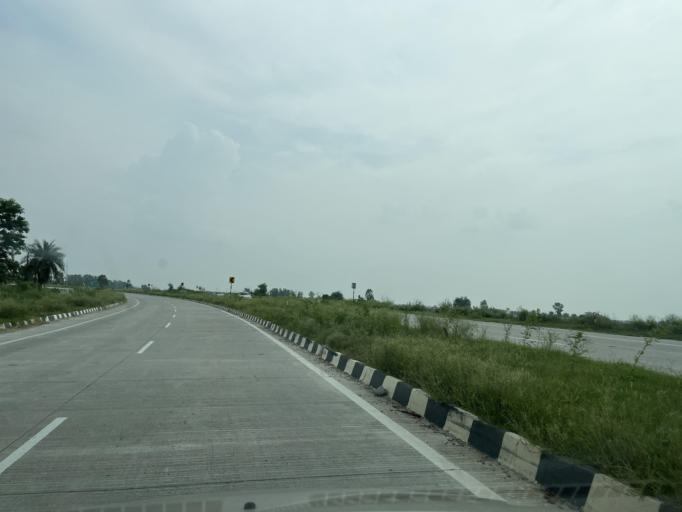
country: IN
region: Uttarakhand
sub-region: Udham Singh Nagar
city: Kashipur
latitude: 29.1792
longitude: 78.9394
